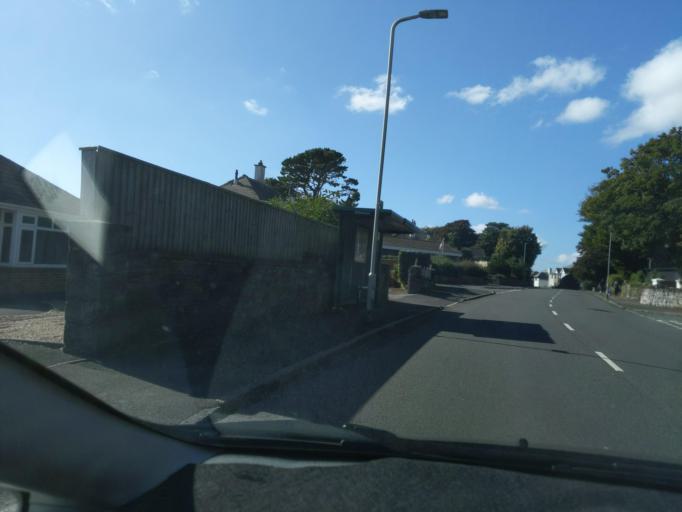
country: GB
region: England
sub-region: Plymouth
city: Plymstock
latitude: 50.3577
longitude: -4.0761
